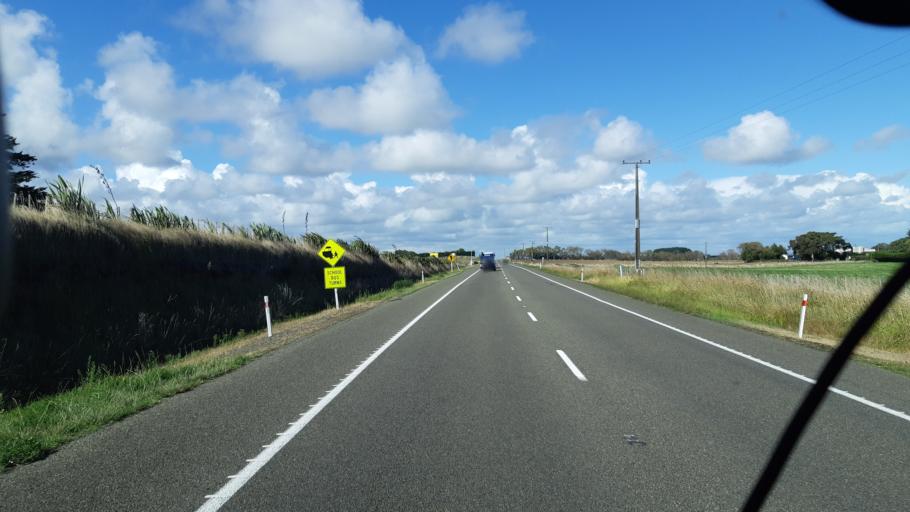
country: NZ
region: Manawatu-Wanganui
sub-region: Wanganui District
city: Wanganui
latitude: -39.9757
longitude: 175.1297
